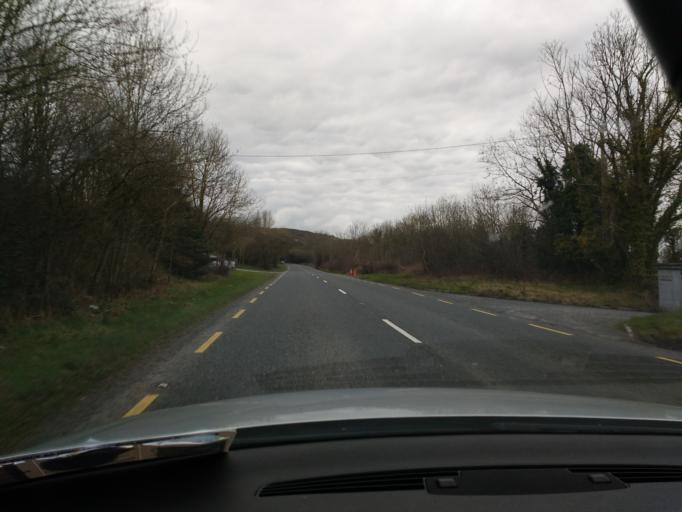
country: IE
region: Leinster
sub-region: Kilkenny
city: Kilkenny
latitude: 52.6927
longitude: -7.2824
